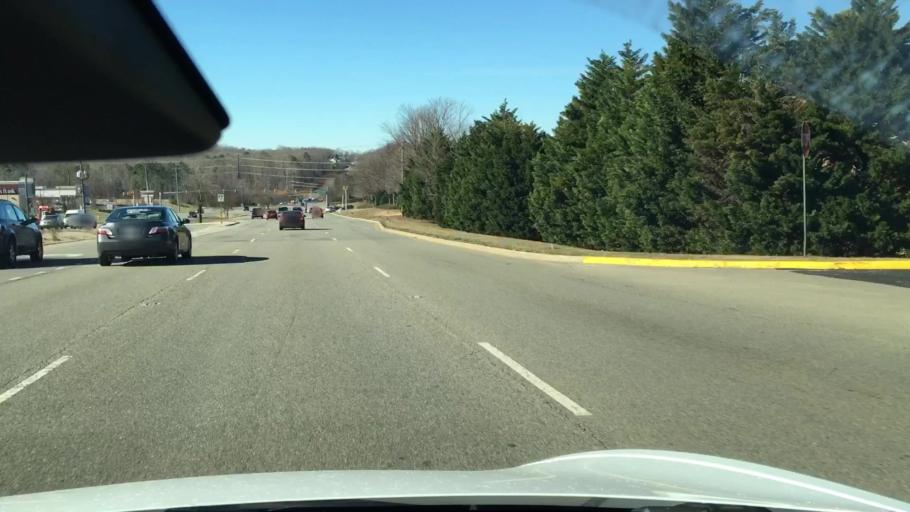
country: US
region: Virginia
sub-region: Chesterfield County
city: Bon Air
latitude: 37.5042
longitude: -77.6249
